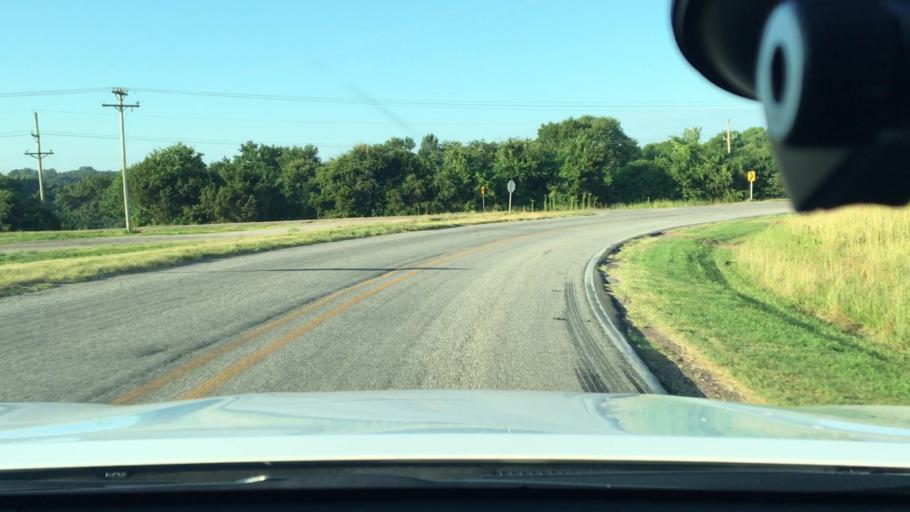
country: US
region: Arkansas
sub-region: Johnson County
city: Coal Hill
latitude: 35.3376
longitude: -93.6036
